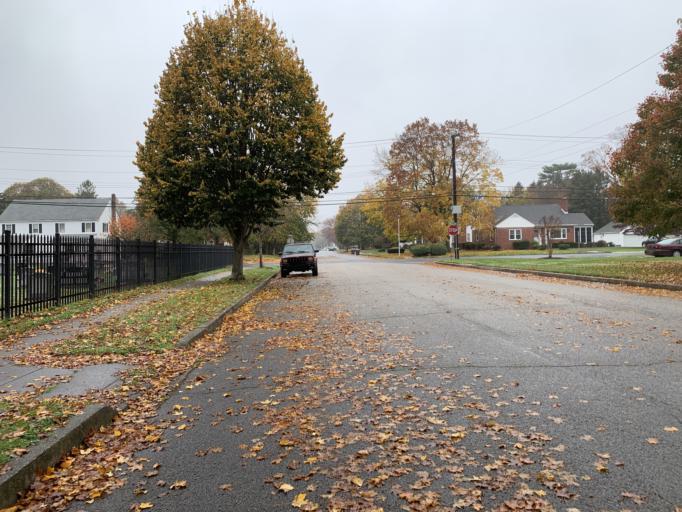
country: US
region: Delaware
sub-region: Kent County
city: Dover
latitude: 39.1677
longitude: -75.5321
